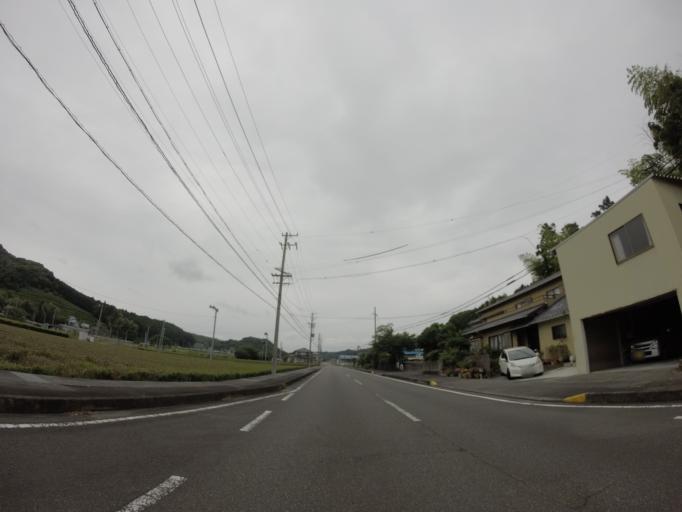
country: JP
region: Shizuoka
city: Shimada
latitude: 34.8025
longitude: 138.1918
